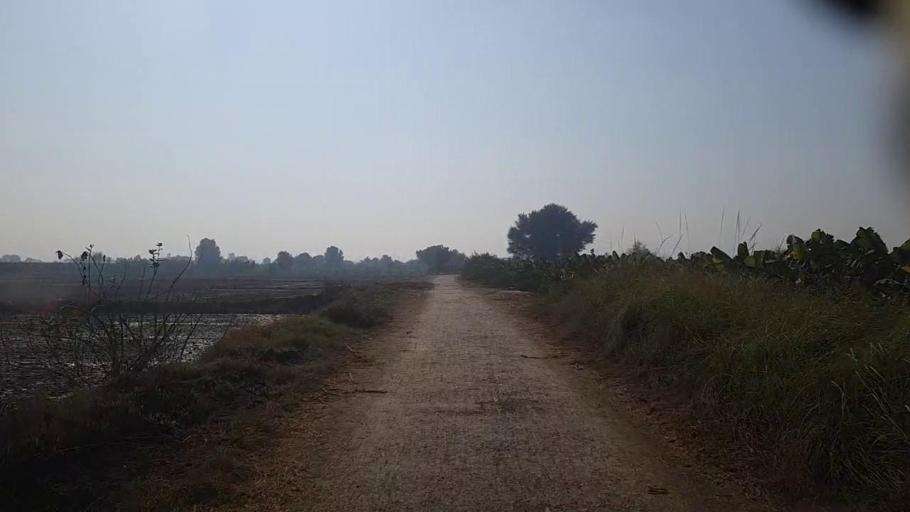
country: PK
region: Sindh
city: Kandiari
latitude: 27.0201
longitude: 68.5038
